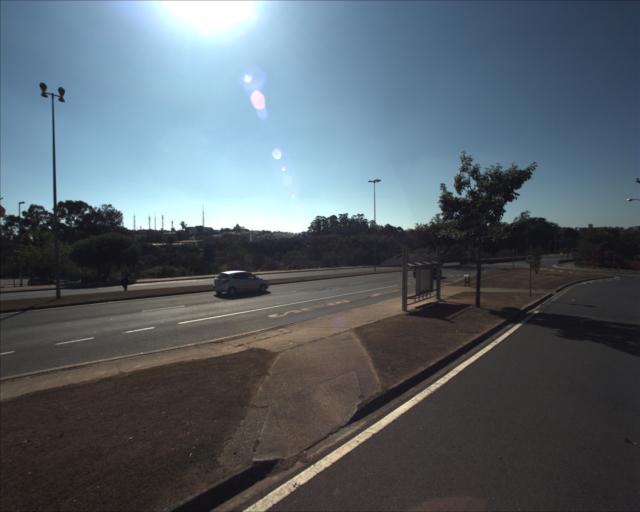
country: BR
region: Sao Paulo
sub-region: Sorocaba
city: Sorocaba
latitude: -23.4891
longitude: -47.4252
